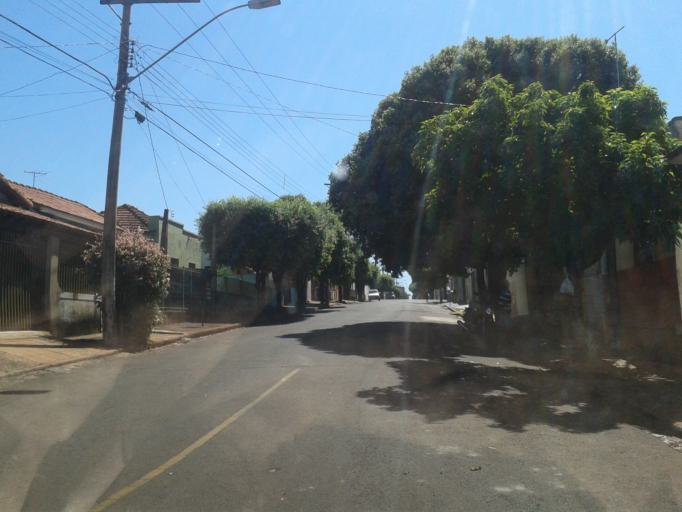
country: BR
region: Minas Gerais
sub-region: Ituiutaba
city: Ituiutaba
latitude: -18.9814
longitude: -49.4704
